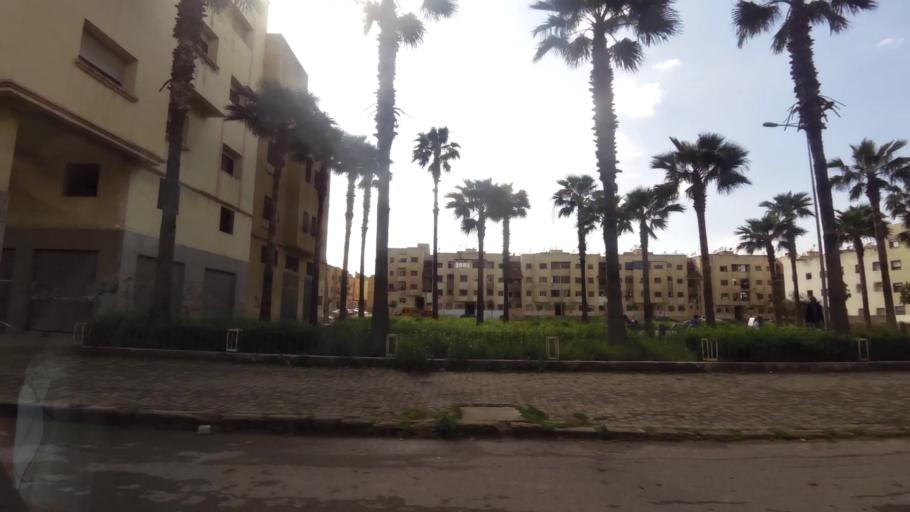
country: MA
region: Chaouia-Ouardigha
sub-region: Settat Province
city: Berrechid
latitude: 33.2604
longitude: -7.5688
